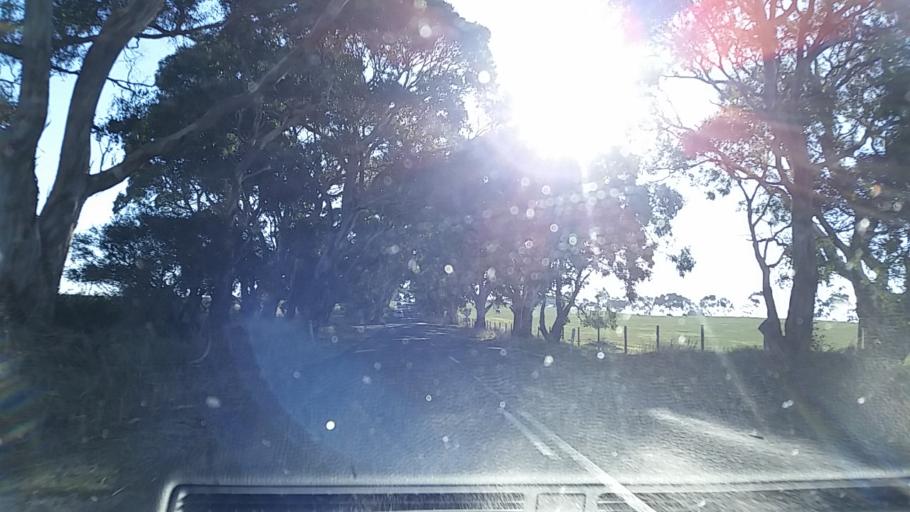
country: AU
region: South Australia
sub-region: Mount Barker
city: Mount Barker
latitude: -35.1291
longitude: 138.9100
